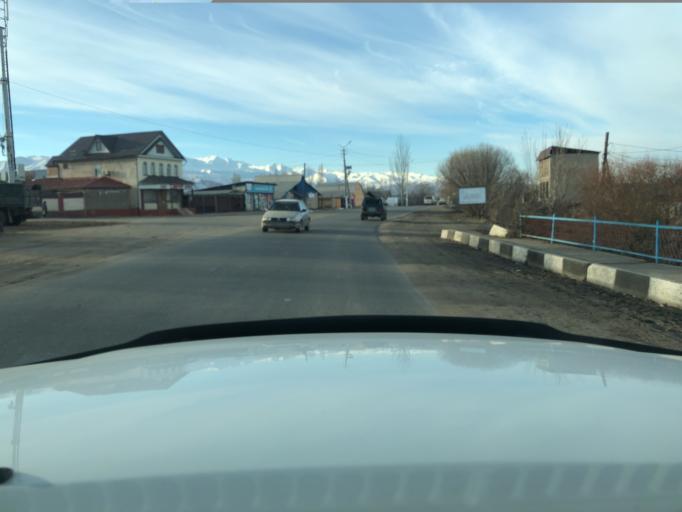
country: KG
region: Ysyk-Koel
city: Pokrovka
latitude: 42.3463
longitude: 78.0133
